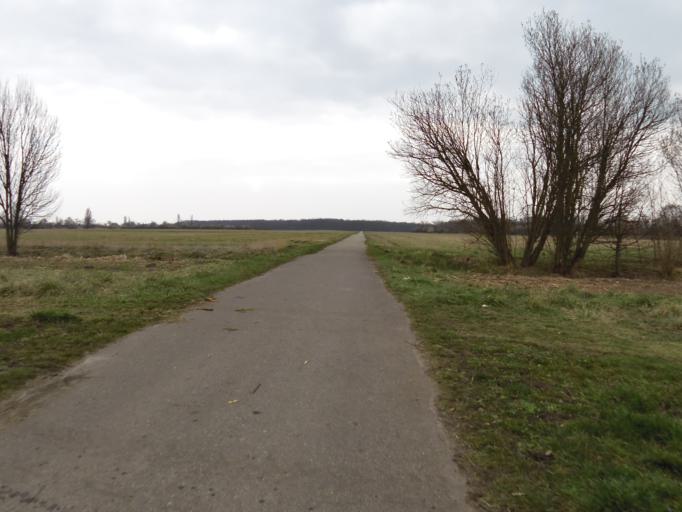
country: DE
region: Rheinland-Pfalz
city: Birkenheide
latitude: 49.4840
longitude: 8.2486
